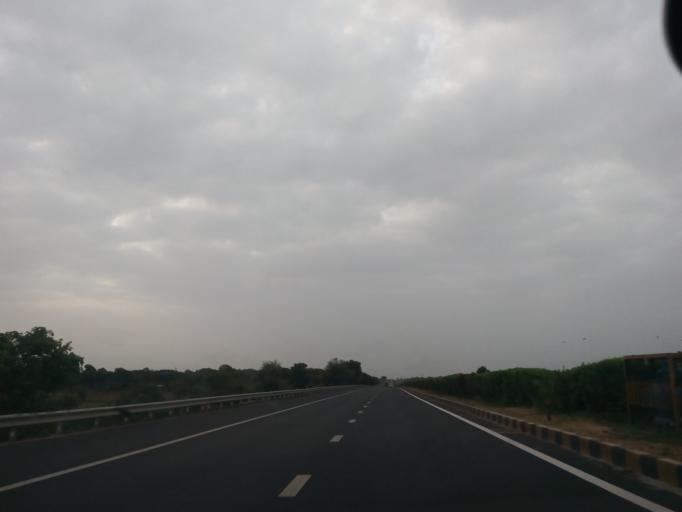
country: IN
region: Gujarat
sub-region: Ahmadabad
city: Naroda
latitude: 22.9587
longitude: 72.6810
